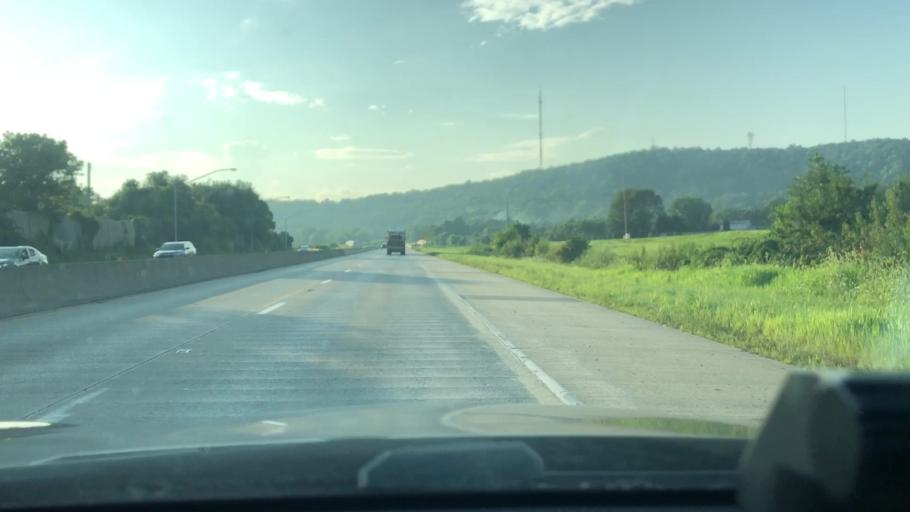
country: US
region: Pennsylvania
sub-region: Lehigh County
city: Coopersburg
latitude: 40.5520
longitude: -75.4287
